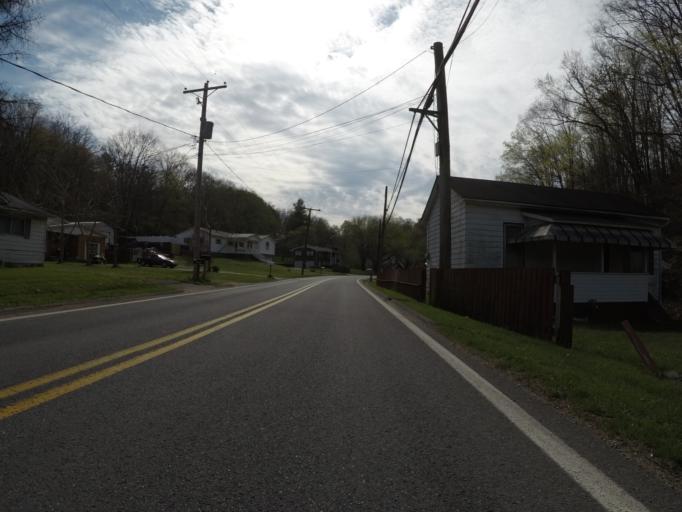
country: US
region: West Virginia
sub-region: Cabell County
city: Pea Ridge
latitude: 38.3763
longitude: -82.3720
